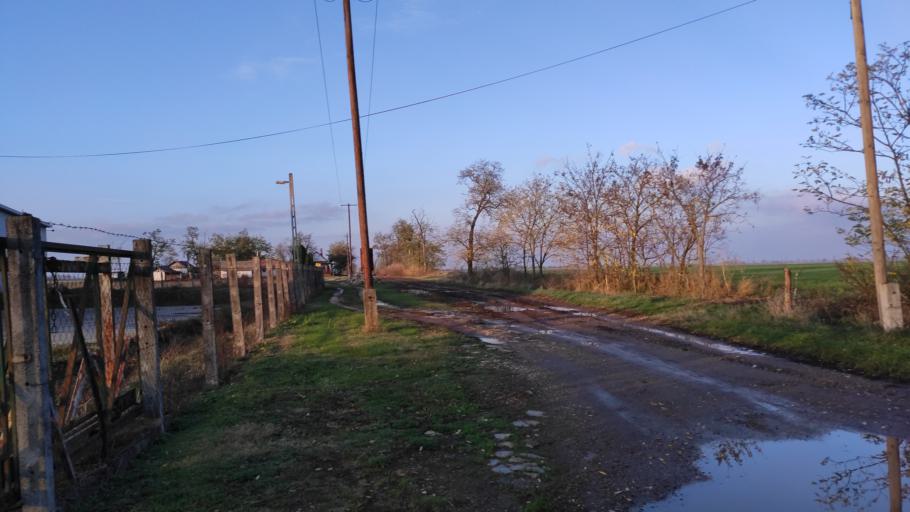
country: HU
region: Bekes
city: Mezobereny
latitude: 46.7661
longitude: 21.0446
